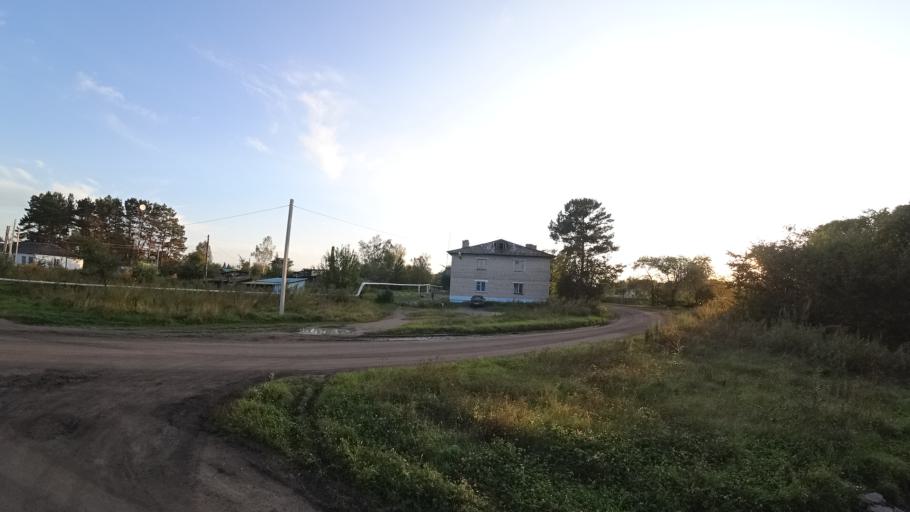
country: RU
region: Amur
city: Arkhara
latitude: 49.3638
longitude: 130.1206
